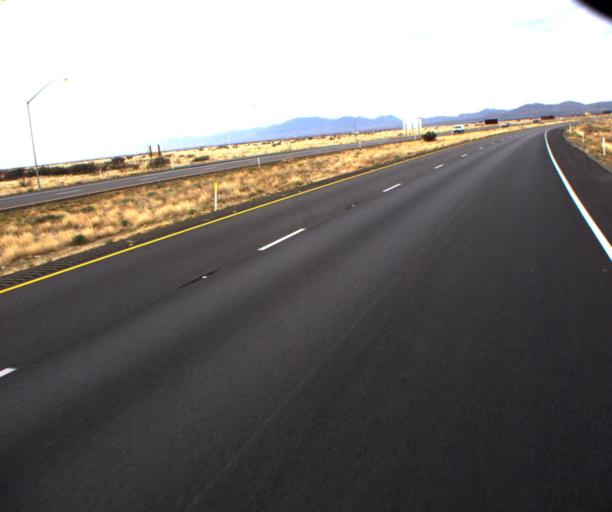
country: US
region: Arizona
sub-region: Cochise County
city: Willcox
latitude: 32.2172
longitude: -109.8826
